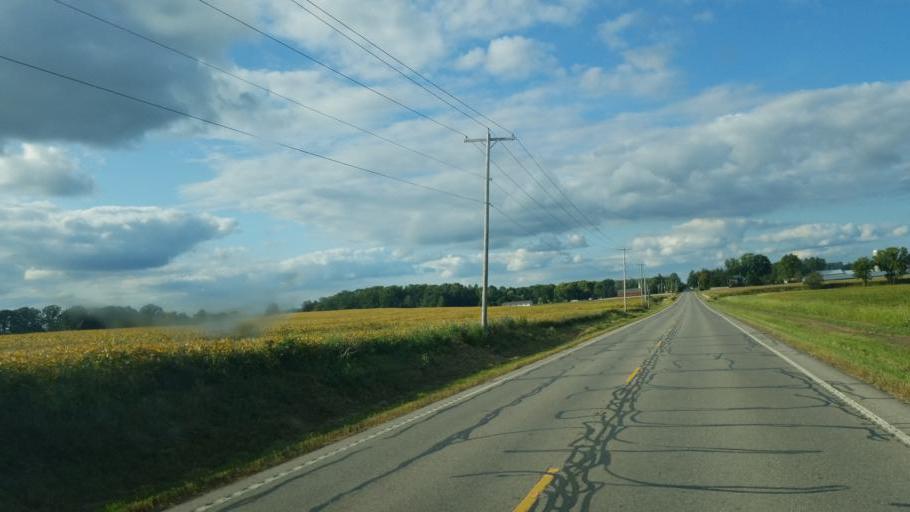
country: US
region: Ohio
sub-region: Richland County
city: Lincoln Heights
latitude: 40.8587
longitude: -82.5134
